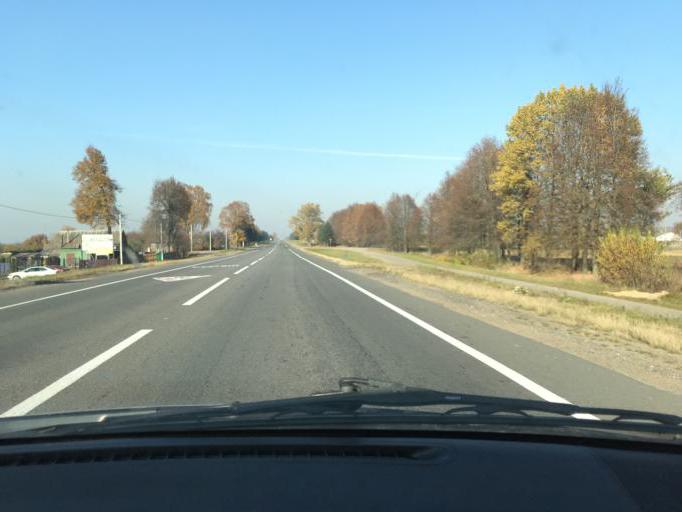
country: BY
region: Mogilev
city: Shklow
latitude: 54.2556
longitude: 30.4505
